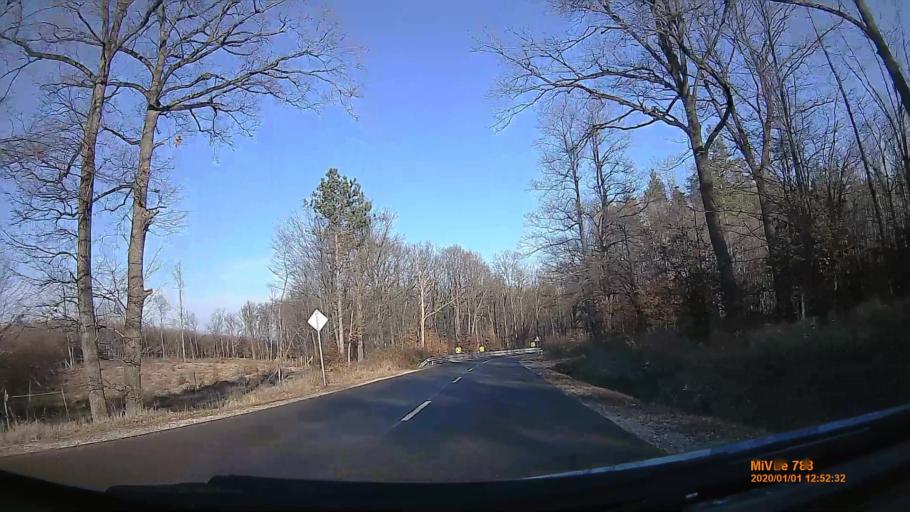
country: HU
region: Heves
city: Paradsasvar
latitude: 47.9022
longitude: 19.9889
